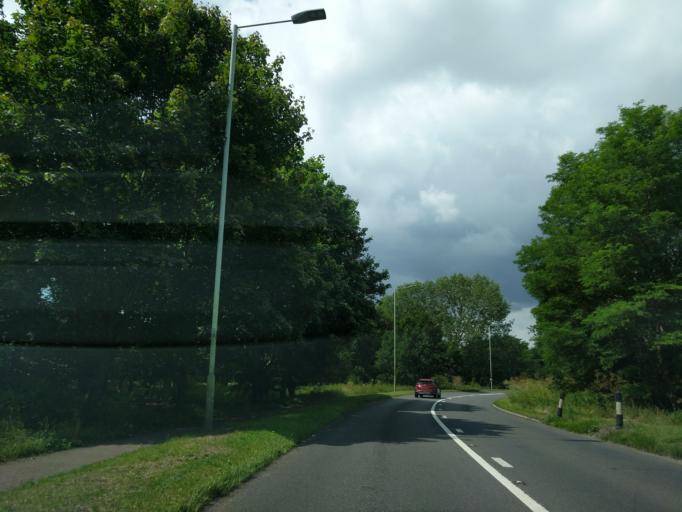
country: GB
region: England
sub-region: Suffolk
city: Lakenheath
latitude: 52.3406
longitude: 0.5289
